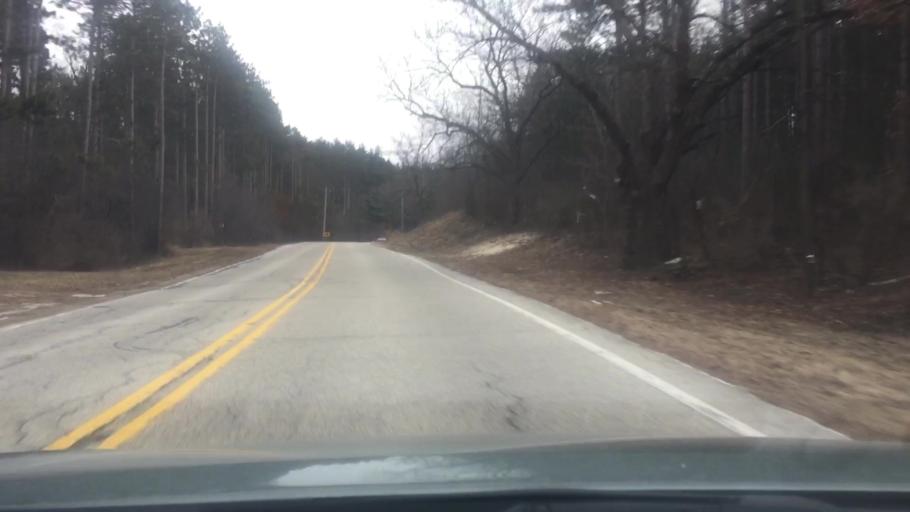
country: US
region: Wisconsin
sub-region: Waukesha County
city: North Prairie
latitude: 42.9426
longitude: -88.4483
